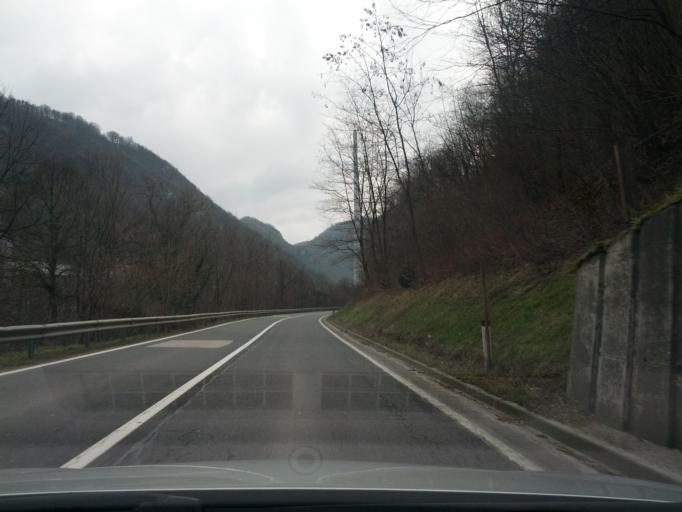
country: SI
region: Trbovlje
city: Trbovlje
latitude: 46.1267
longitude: 15.0443
